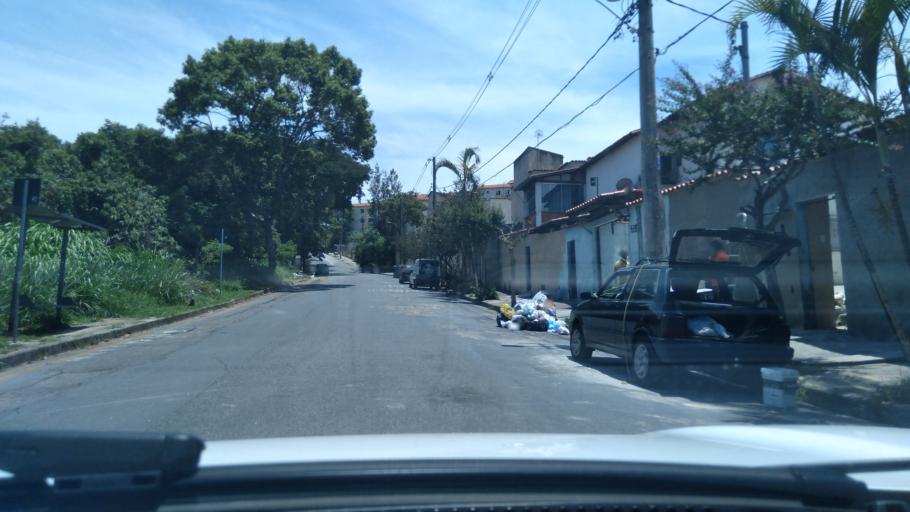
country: BR
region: Minas Gerais
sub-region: Contagem
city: Contagem
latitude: -19.9287
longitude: -44.0174
